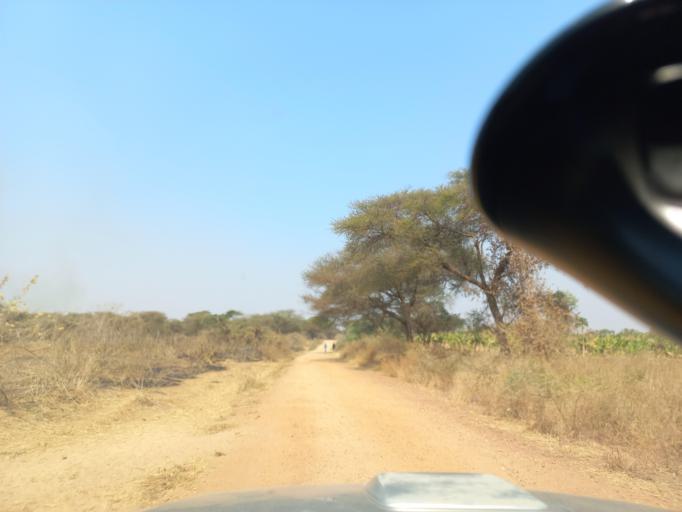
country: ZW
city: Chirundu
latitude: -15.9408
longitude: 28.8235
